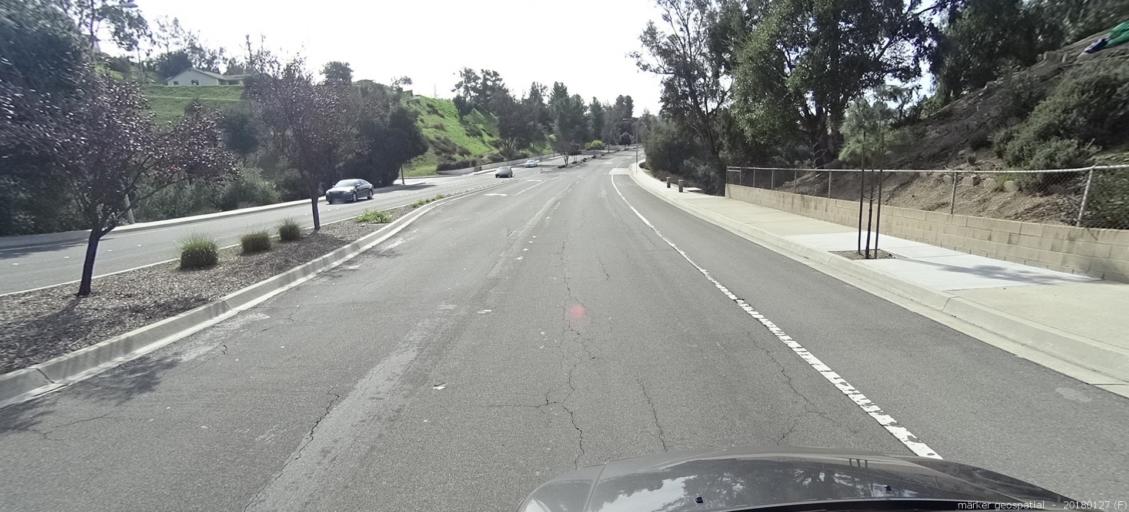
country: US
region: California
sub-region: Los Angeles County
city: Diamond Bar
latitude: 34.0075
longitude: -117.8082
